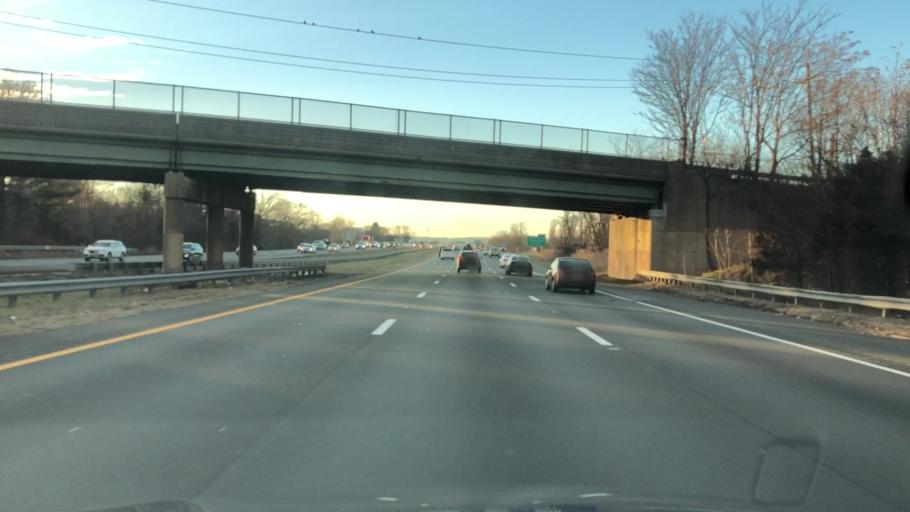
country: US
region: New Jersey
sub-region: Middlesex County
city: Edison
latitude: 40.5471
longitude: -74.4003
